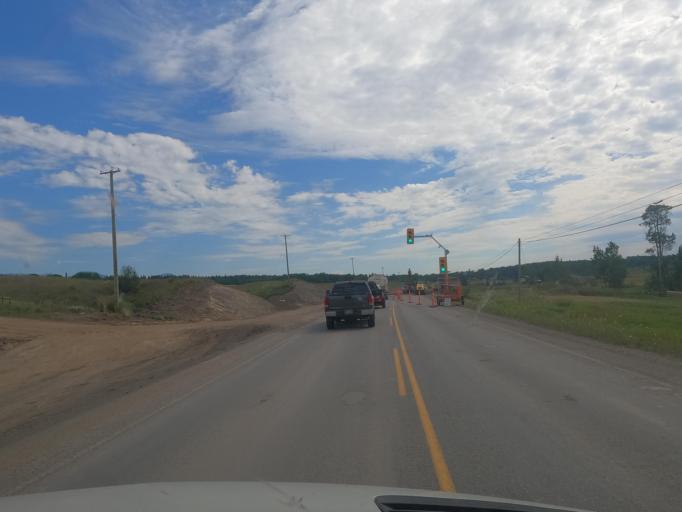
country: CA
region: British Columbia
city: Smithers
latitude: 54.8662
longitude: -127.2349
